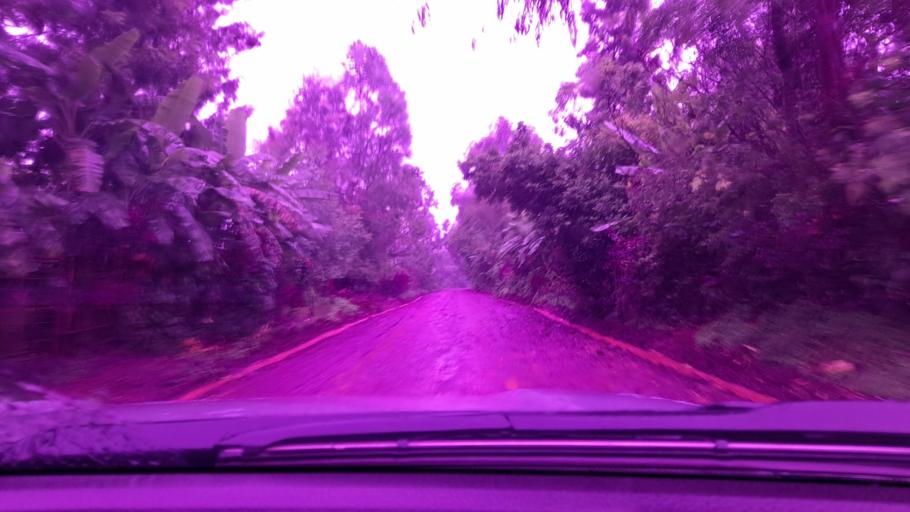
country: ET
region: Oromiya
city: Metu
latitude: 8.3397
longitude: 35.6029
